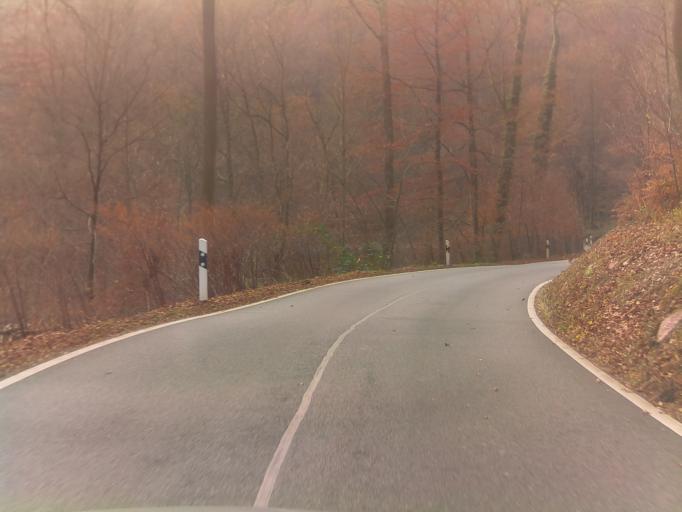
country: DE
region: Baden-Wuerttemberg
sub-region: Karlsruhe Region
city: Gaiberg
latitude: 49.3892
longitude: 8.7470
